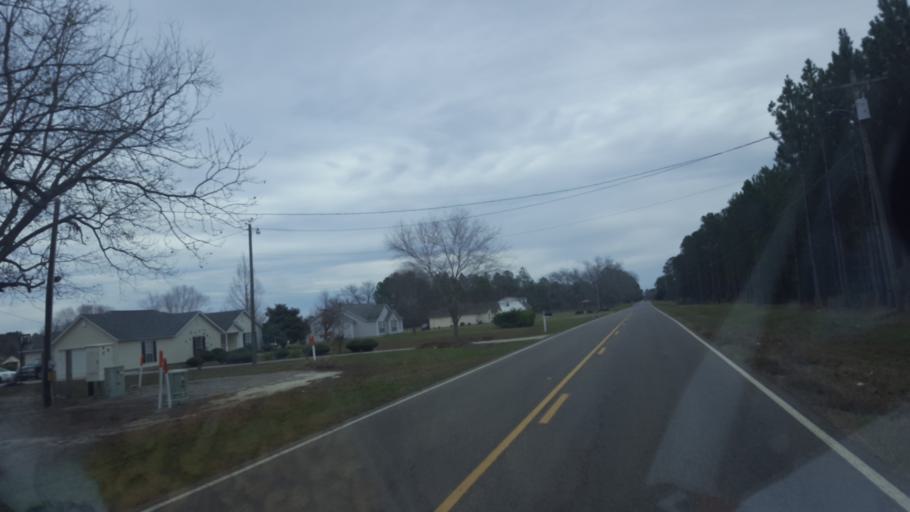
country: US
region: Georgia
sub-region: Ben Hill County
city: Fitzgerald
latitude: 31.7435
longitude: -83.2893
